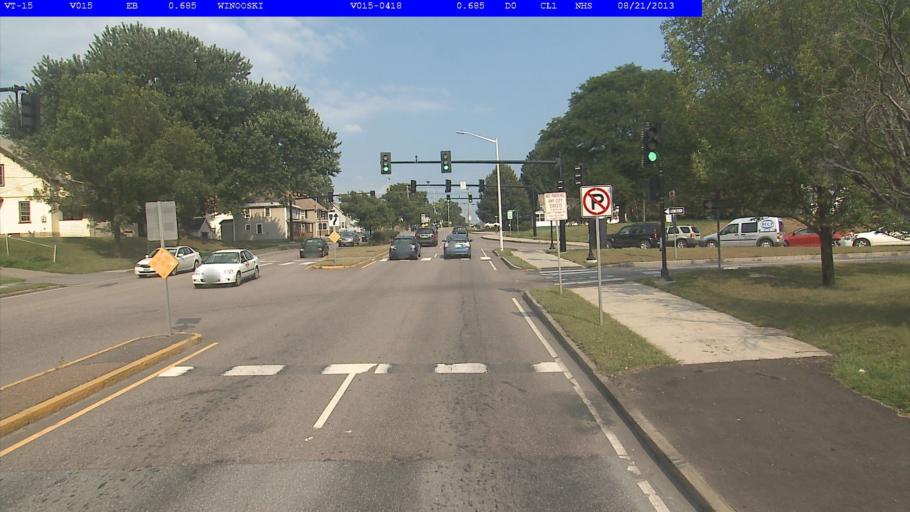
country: US
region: Vermont
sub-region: Chittenden County
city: Winooski
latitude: 44.4932
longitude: -73.1730
